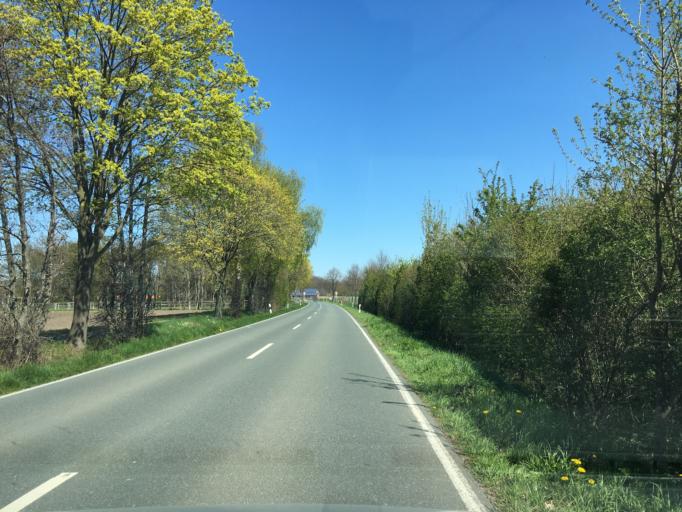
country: DE
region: North Rhine-Westphalia
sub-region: Regierungsbezirk Munster
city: Sudlohn
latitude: 51.9373
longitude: 6.8338
